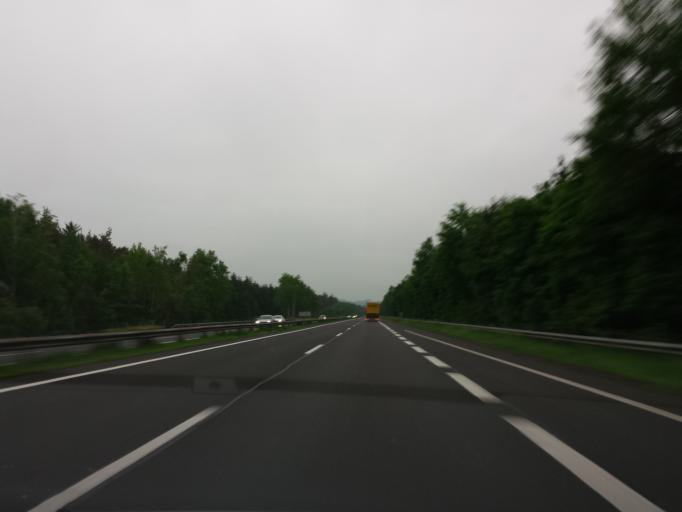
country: AT
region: Styria
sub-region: Politischer Bezirk Hartberg-Fuerstenfeld
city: Hainersdorf
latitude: 47.1143
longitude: 15.9846
